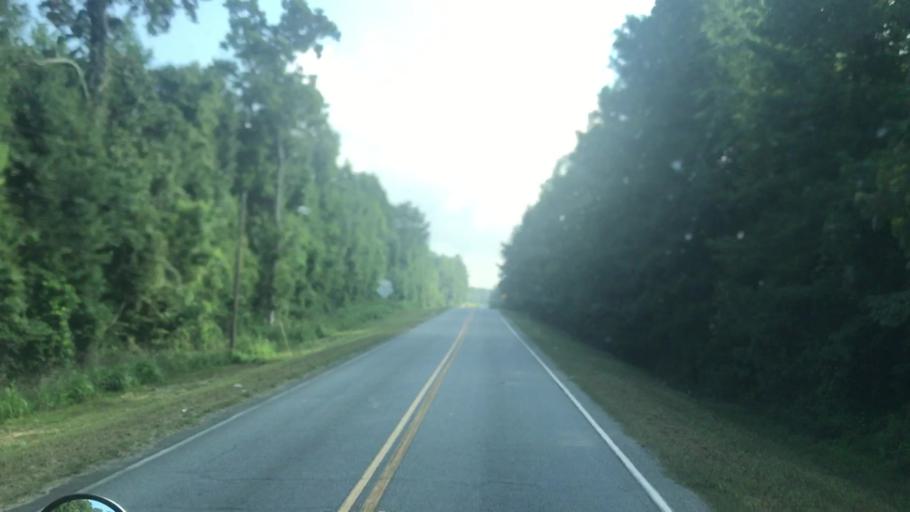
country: US
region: Florida
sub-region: Gadsden County
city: Havana
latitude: 30.7206
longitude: -84.4878
